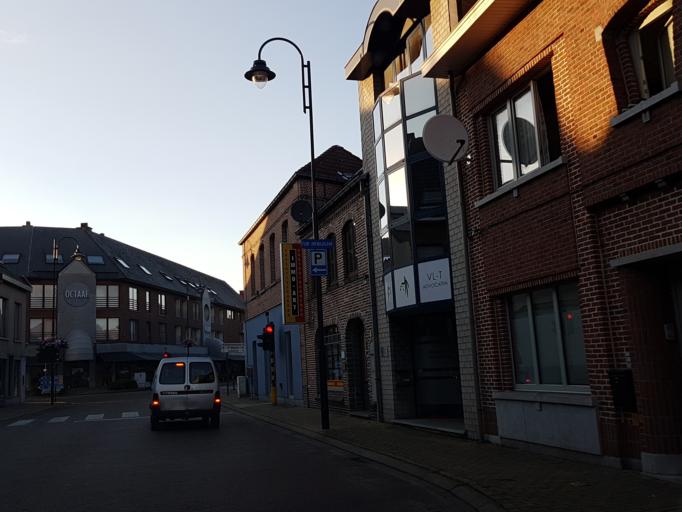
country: BE
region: Flanders
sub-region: Provincie Oost-Vlaanderen
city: Lebbeke
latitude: 50.9997
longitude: 4.1283
